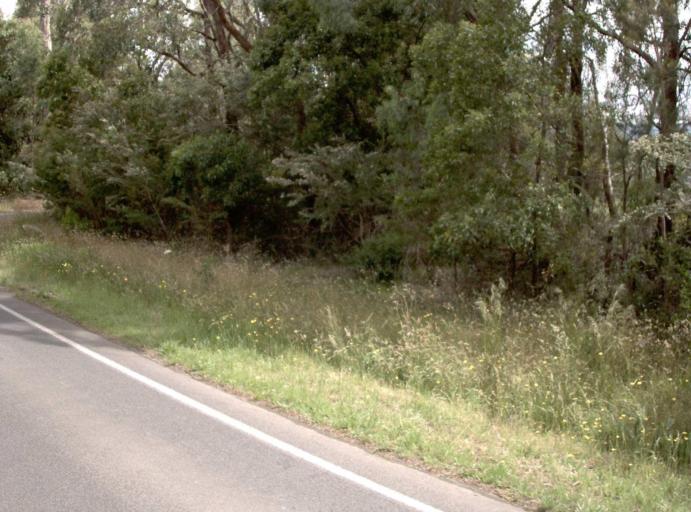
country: AU
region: Victoria
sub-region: Latrobe
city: Moe
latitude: -38.0842
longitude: 146.1967
